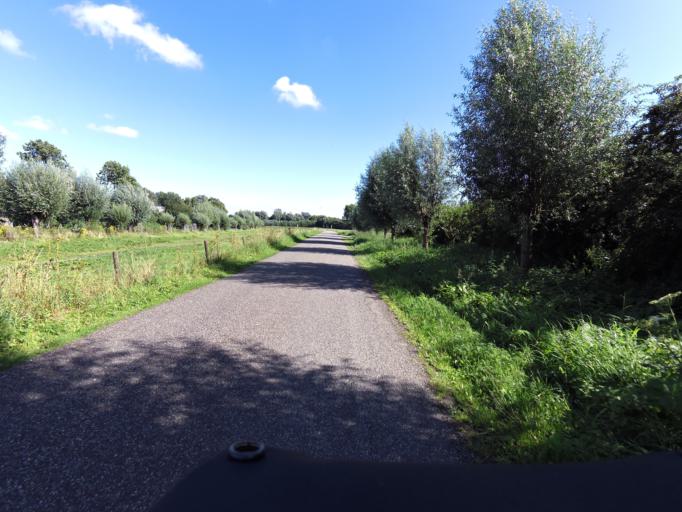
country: NL
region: South Holland
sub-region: Gemeente Spijkenisse
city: Spijkenisse
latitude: 51.8518
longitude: 4.2962
